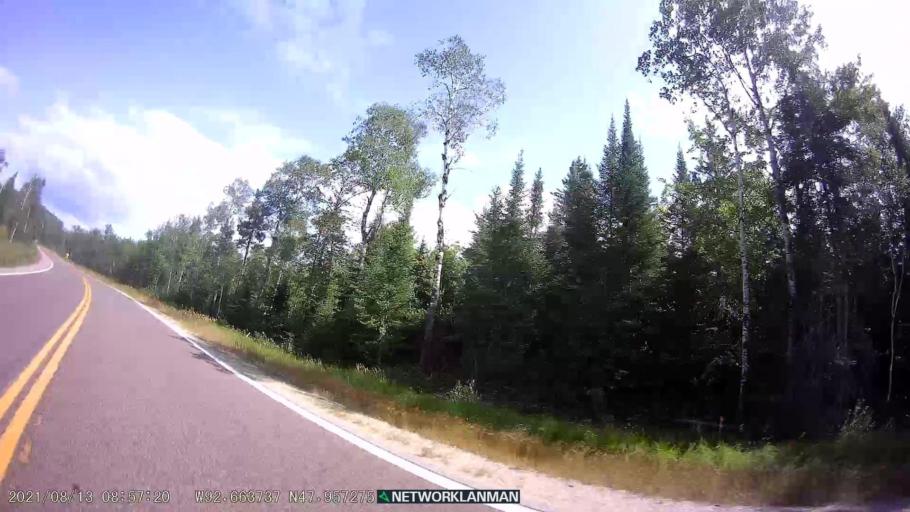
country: US
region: Minnesota
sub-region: Saint Louis County
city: Mountain Iron
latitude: 47.9575
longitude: -92.6638
